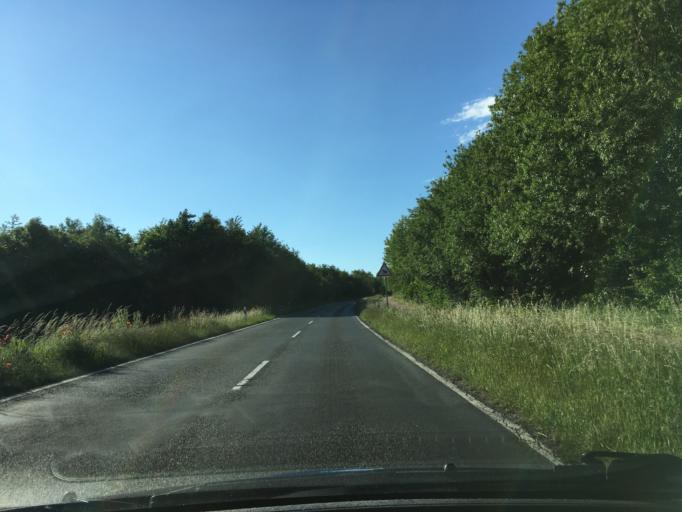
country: DE
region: Lower Saxony
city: Duingen
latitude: 51.9947
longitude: 9.7139
